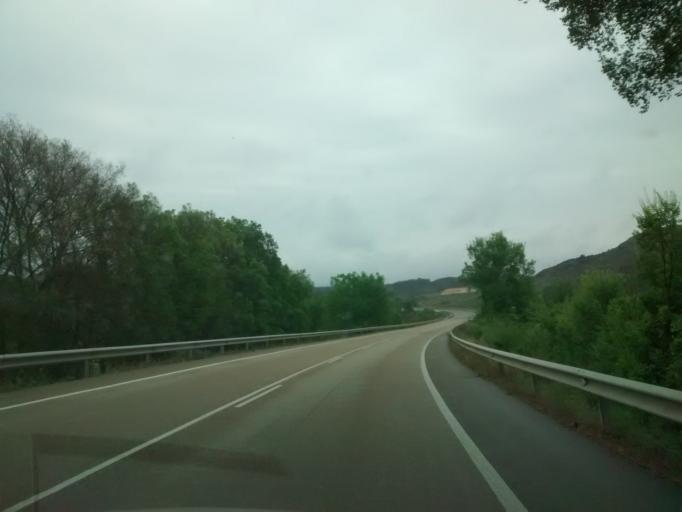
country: ES
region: Aragon
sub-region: Provincia de Zaragoza
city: Caspe
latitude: 41.2113
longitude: 0.0103
